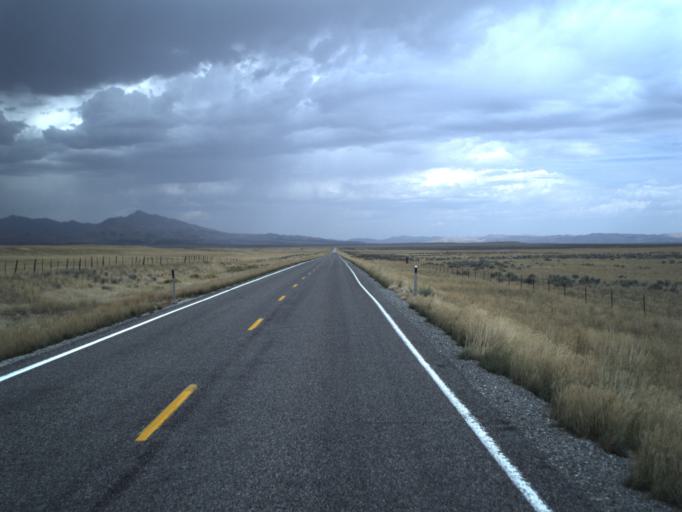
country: US
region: Idaho
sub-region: Oneida County
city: Malad City
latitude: 41.9062
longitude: -113.1033
